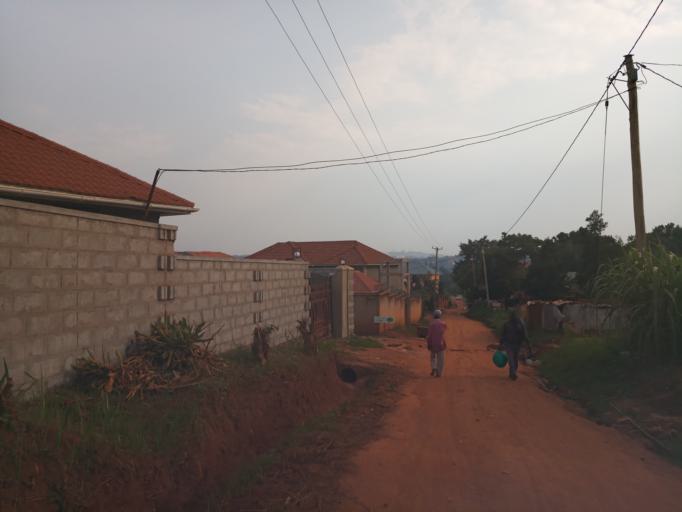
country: UG
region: Central Region
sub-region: Wakiso District
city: Kireka
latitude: 0.3909
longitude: 32.6393
